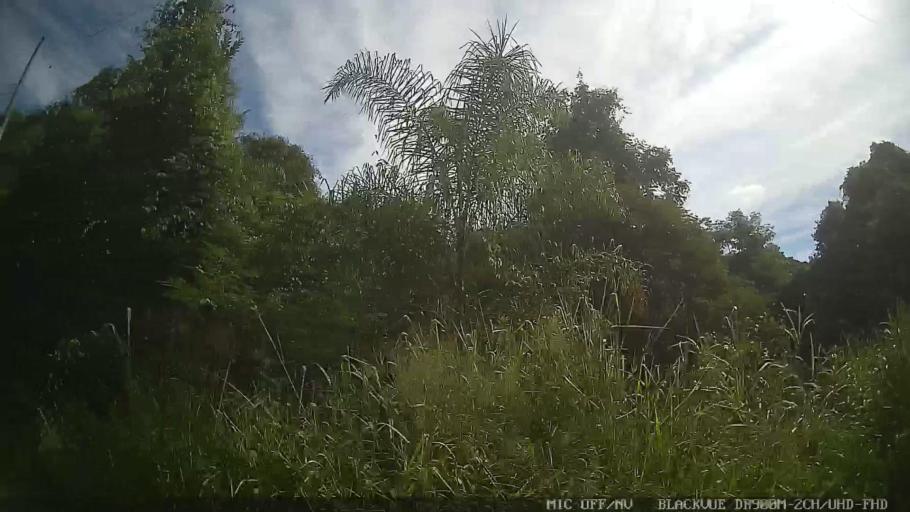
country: BR
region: Sao Paulo
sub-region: Jarinu
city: Jarinu
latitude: -23.0426
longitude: -46.6428
